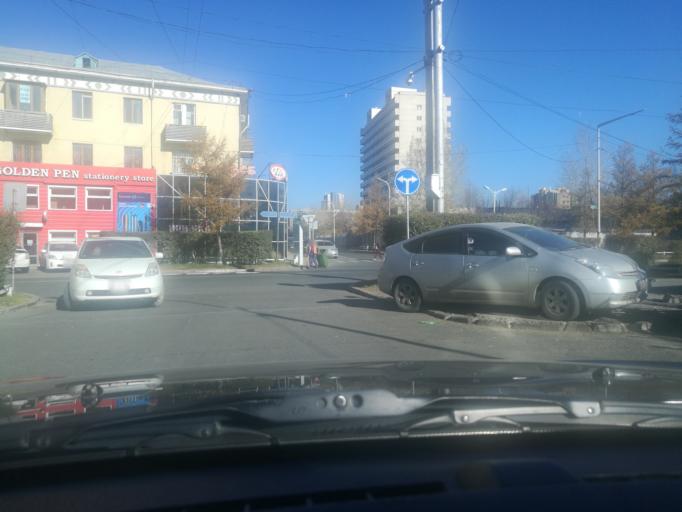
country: MN
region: Ulaanbaatar
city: Ulaanbaatar
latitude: 47.9141
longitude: 106.9091
